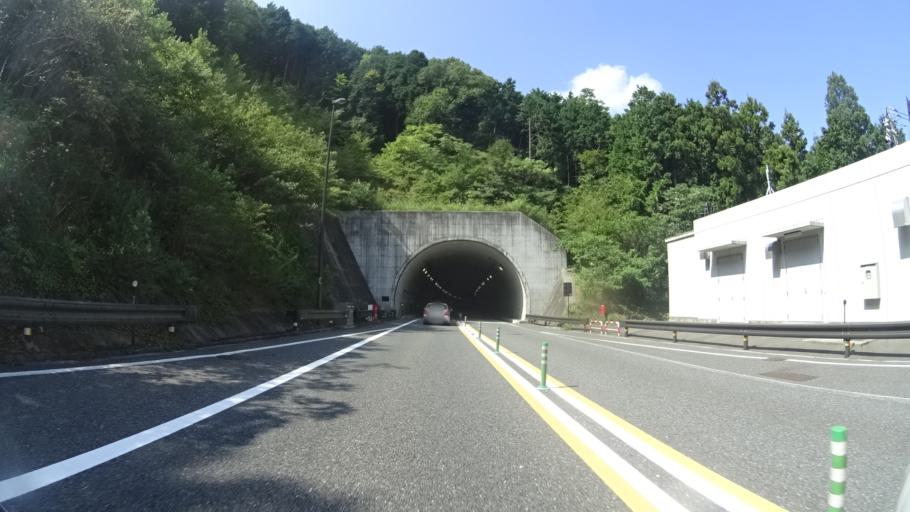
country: JP
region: Shimane
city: Hamada
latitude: 34.8591
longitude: 132.0518
